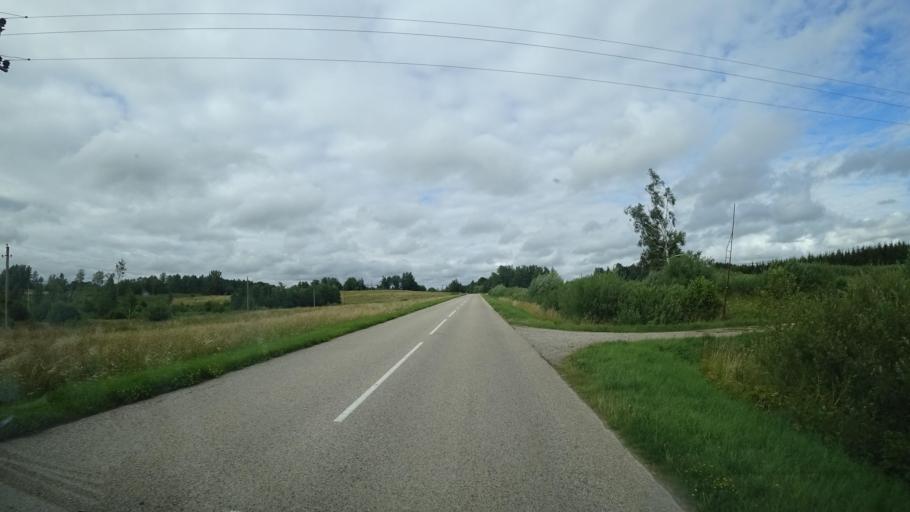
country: LT
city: Virbalis
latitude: 54.4201
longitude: 22.9279
